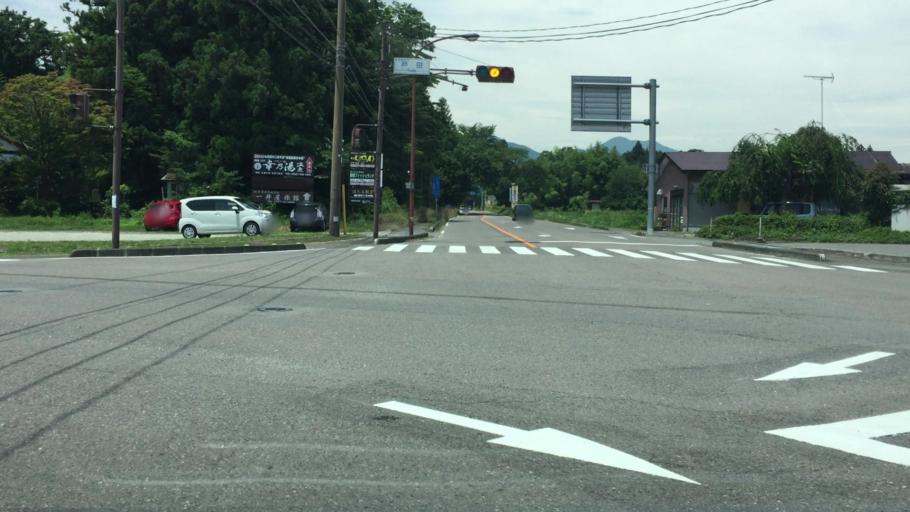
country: JP
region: Tochigi
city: Kuroiso
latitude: 37.0130
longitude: 139.9624
